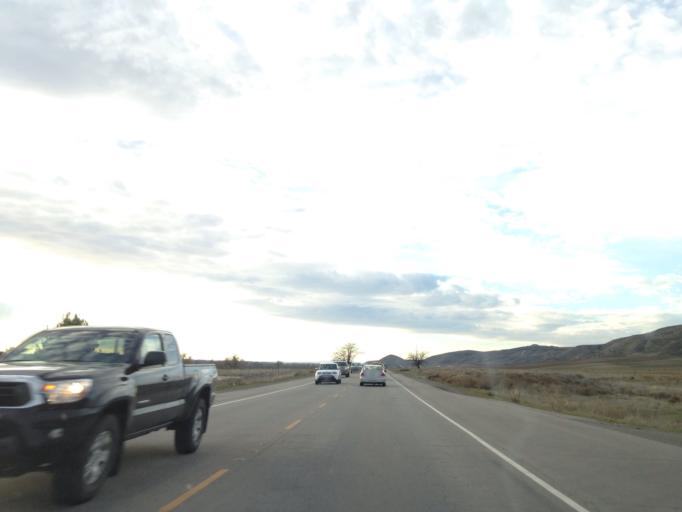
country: US
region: California
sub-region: San Luis Obispo County
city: Shandon
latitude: 35.6624
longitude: -120.3689
